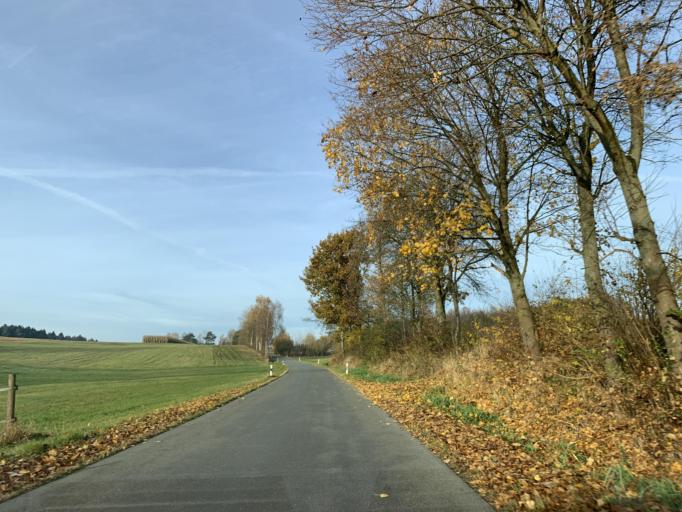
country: DE
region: Bavaria
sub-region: Upper Palatinate
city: Neukirchen-Balbini
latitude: 49.3369
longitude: 12.4371
